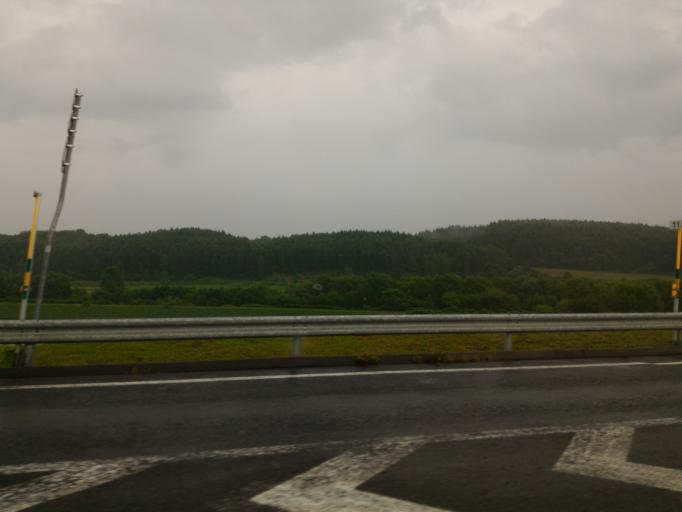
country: JP
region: Hokkaido
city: Nayoro
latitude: 44.4157
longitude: 142.4026
